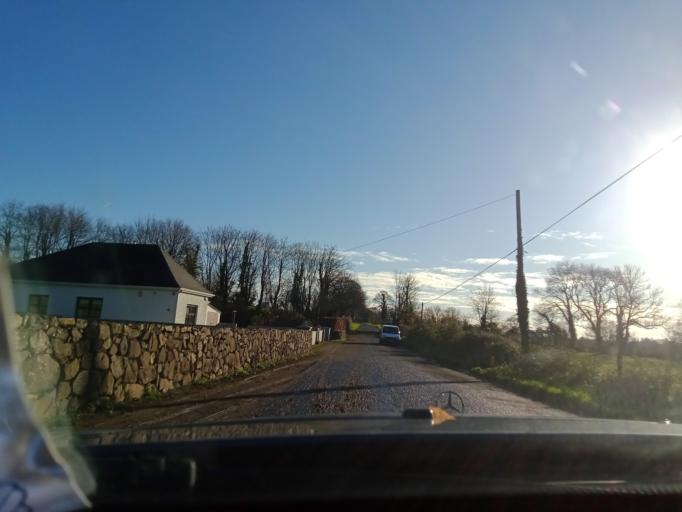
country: IE
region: Leinster
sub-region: Kilkenny
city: Mooncoin
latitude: 52.3394
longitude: -7.2678
